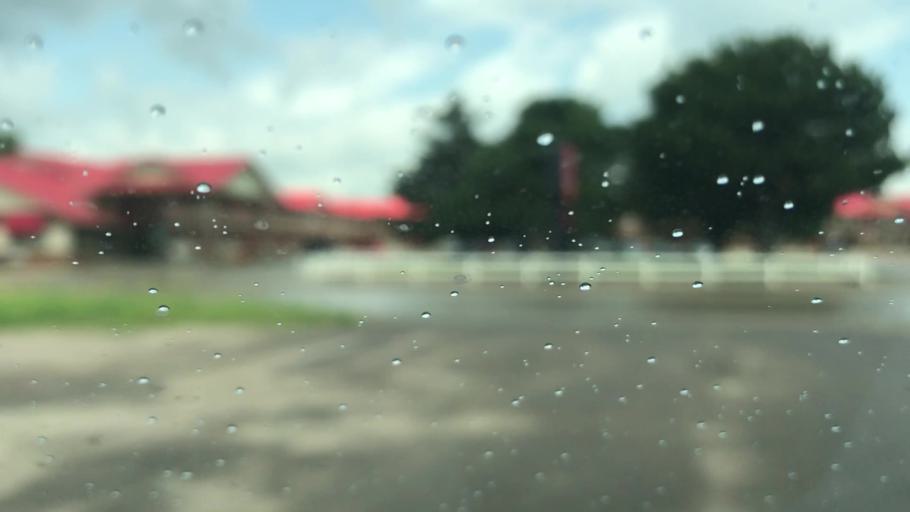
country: US
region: Nebraska
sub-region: Cherry County
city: Valentine
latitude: 42.8676
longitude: -100.5476
